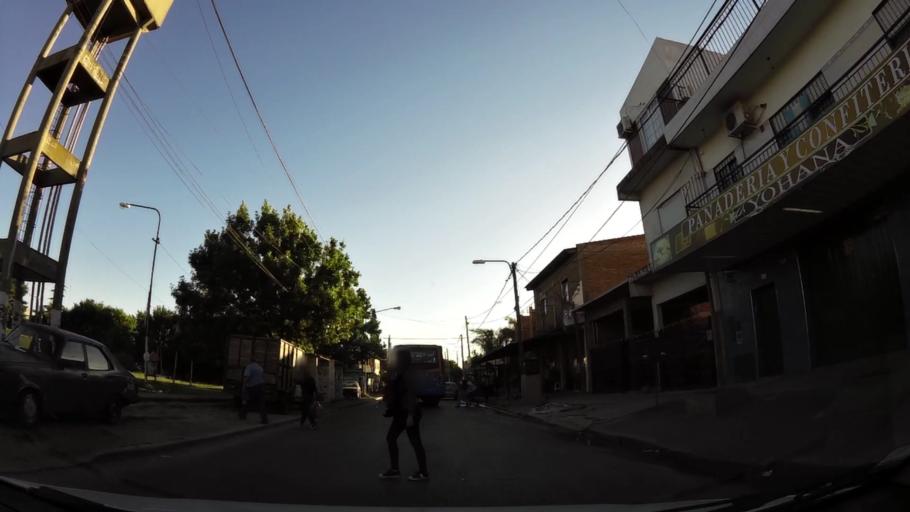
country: AR
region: Buenos Aires
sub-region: Partido de Moron
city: Moron
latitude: -34.7144
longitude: -58.6138
